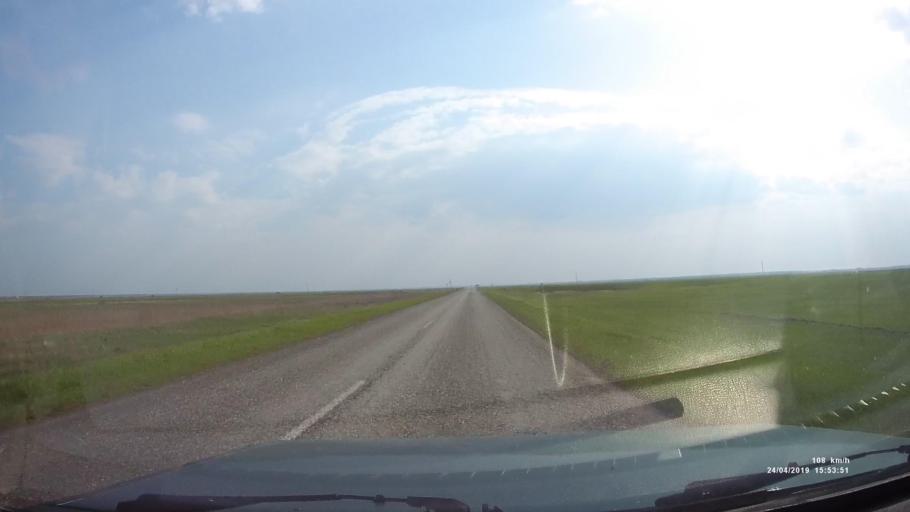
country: RU
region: Kalmykiya
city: Yashalta
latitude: 46.5929
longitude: 42.5703
